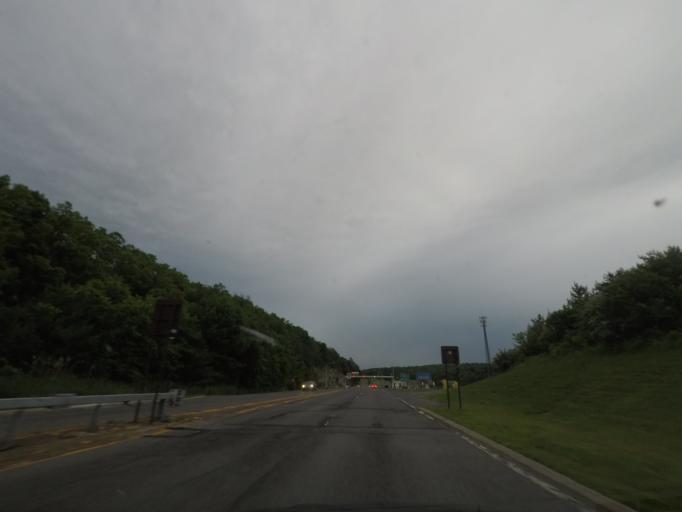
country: US
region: New York
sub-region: Columbia County
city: Chatham
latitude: 42.4159
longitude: -73.5488
